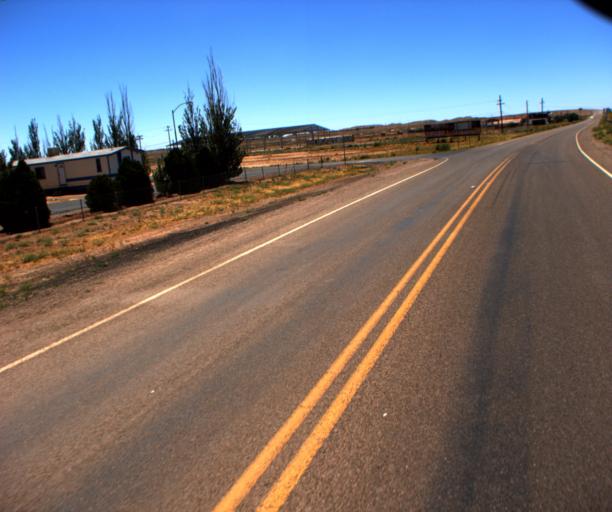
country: US
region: Arizona
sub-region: Coconino County
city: LeChee
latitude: 35.0379
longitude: -110.7314
